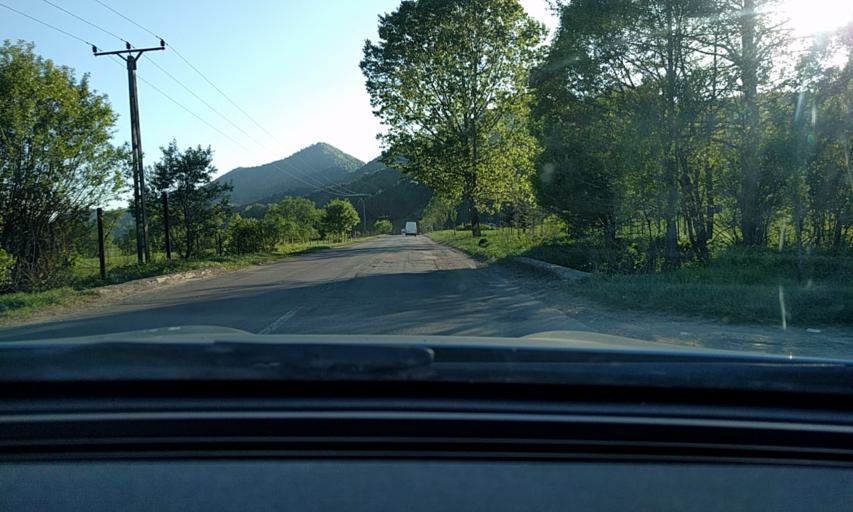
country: RO
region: Bacau
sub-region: Oras Slanic-Moldova
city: Slanic-Moldova
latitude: 46.1810
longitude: 26.4871
